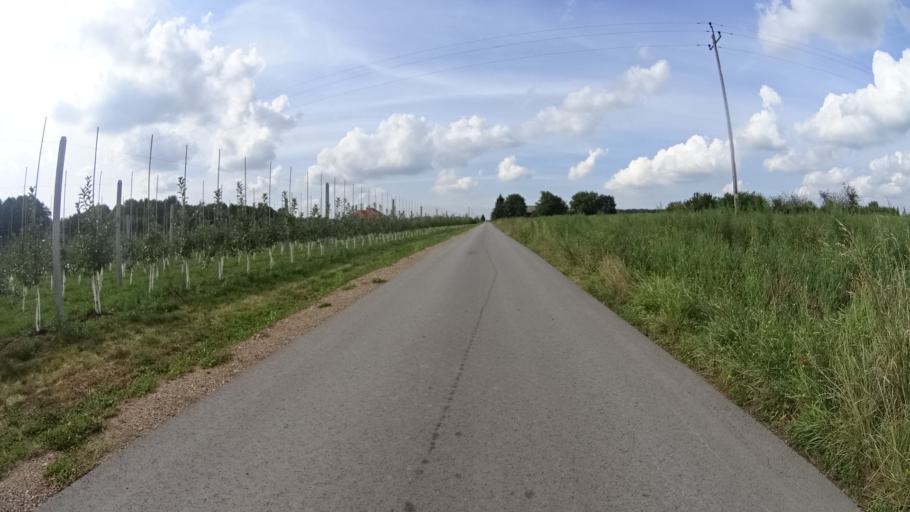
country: PL
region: Masovian Voivodeship
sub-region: Powiat grojecki
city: Goszczyn
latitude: 51.6957
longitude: 20.8216
